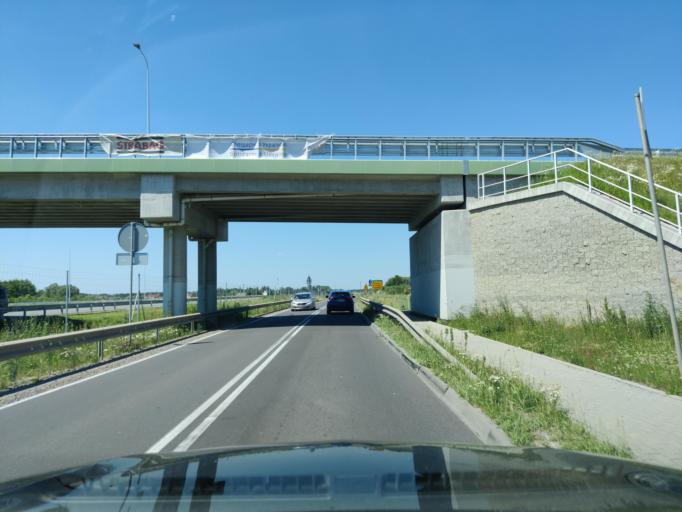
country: PL
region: Masovian Voivodeship
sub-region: Powiat plonski
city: Plonsk
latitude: 52.6960
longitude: 20.3471
